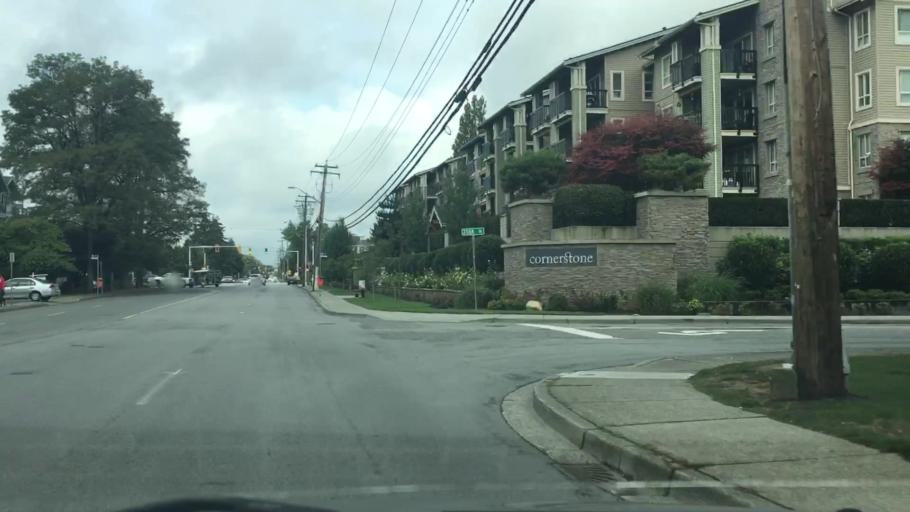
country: CA
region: British Columbia
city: Langley
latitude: 49.1047
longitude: -122.6405
